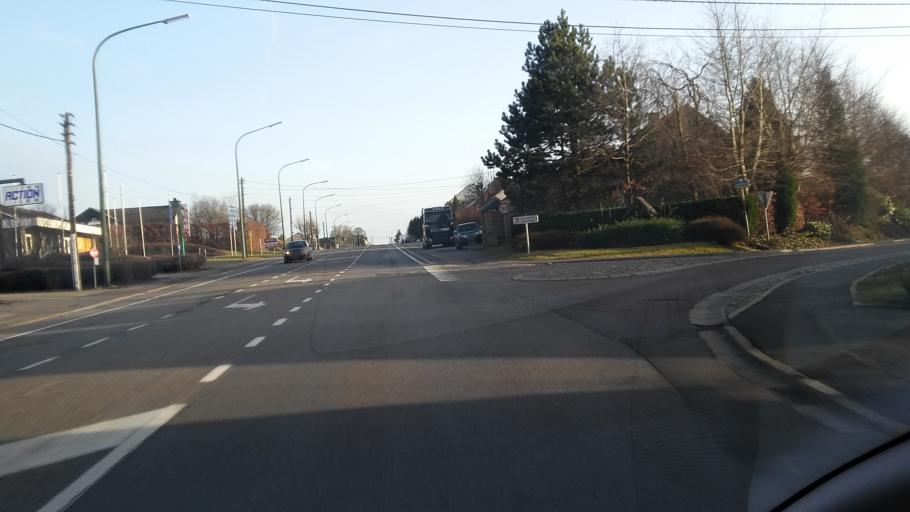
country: BE
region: Wallonia
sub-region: Province du Luxembourg
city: Bastogne
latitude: 49.9961
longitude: 5.7181
